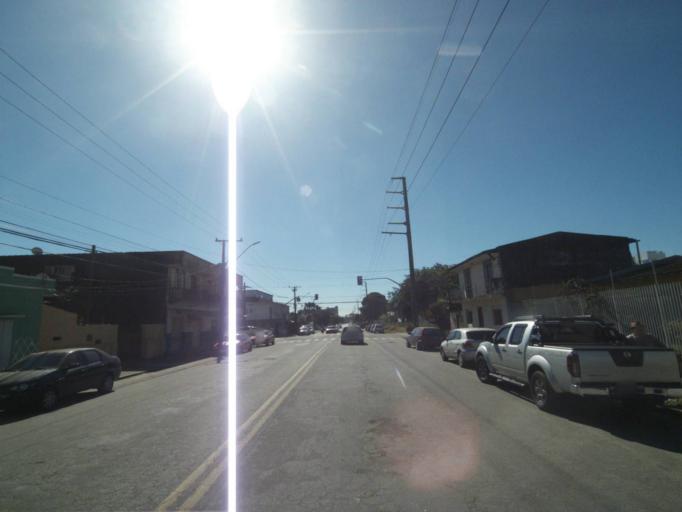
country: BR
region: Parana
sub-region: Paranagua
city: Paranagua
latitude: -25.5167
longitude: -48.5154
